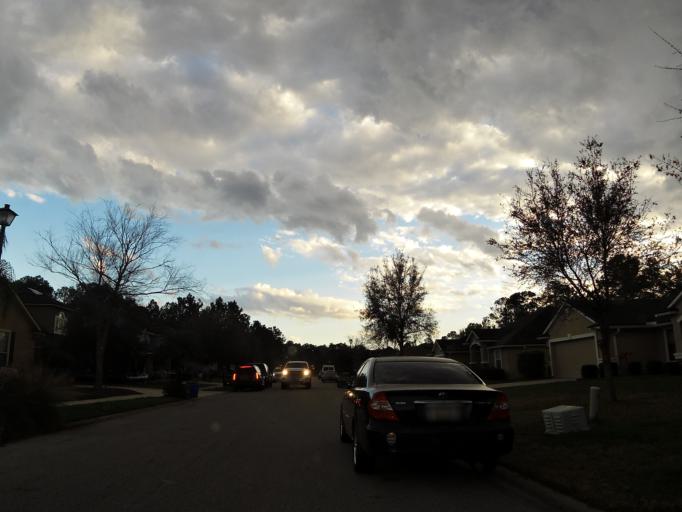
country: US
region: Florida
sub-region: Saint Johns County
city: Fruit Cove
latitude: 30.1717
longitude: -81.5776
